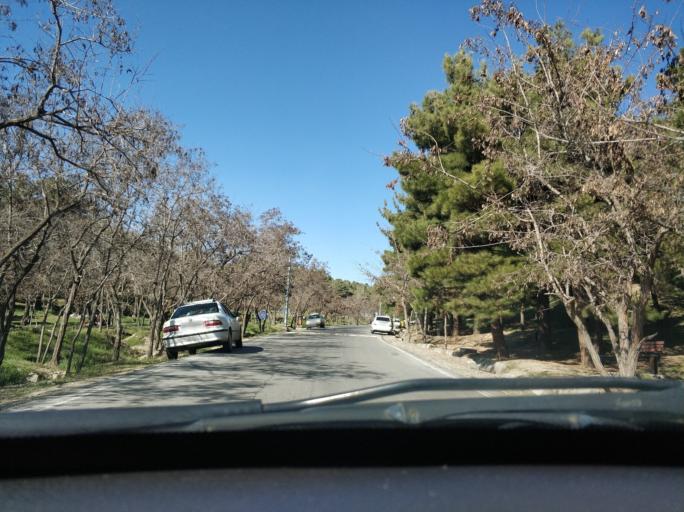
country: IR
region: Tehran
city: Tajrish
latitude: 35.7891
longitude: 51.5599
